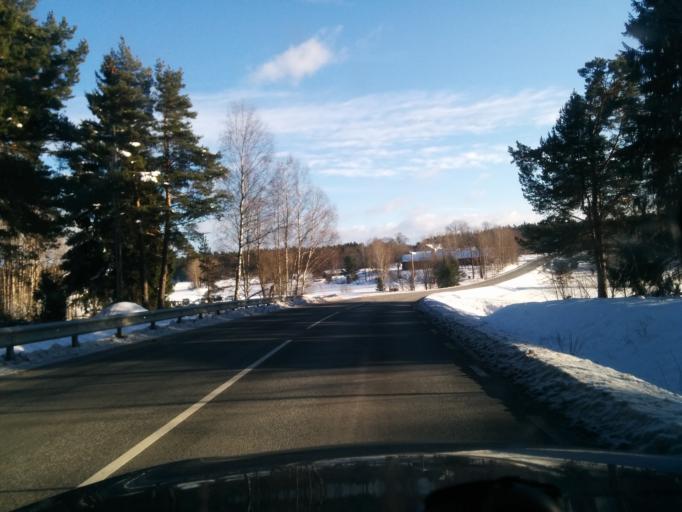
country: SE
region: Stockholm
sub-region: Taby Kommun
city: Taby
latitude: 59.4869
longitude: 18.0817
